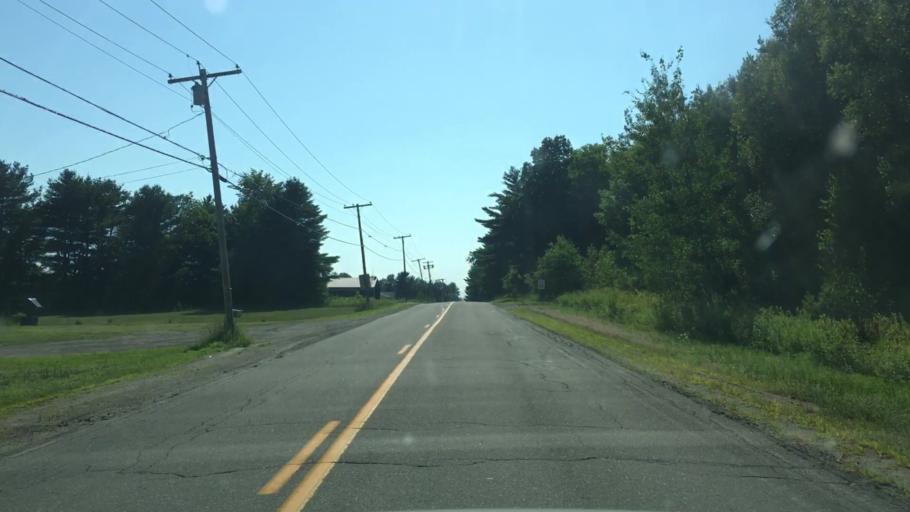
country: US
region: Maine
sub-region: Penobscot County
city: Enfield
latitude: 45.2474
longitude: -68.5939
